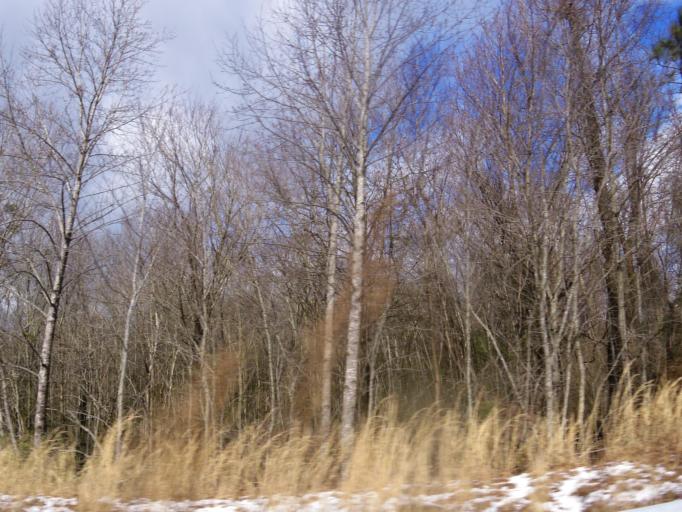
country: US
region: North Carolina
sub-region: Wilson County
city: Lucama
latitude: 35.7118
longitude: -77.9958
